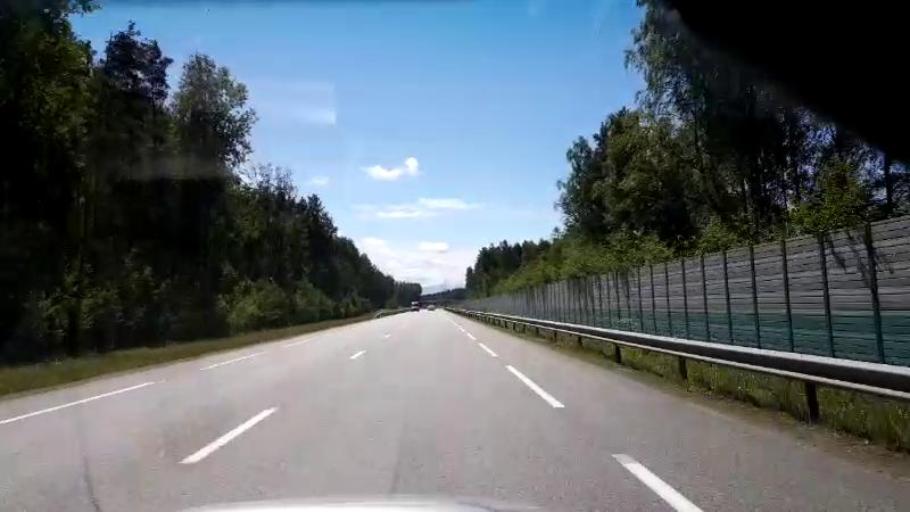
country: LV
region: Saulkrastu
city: Saulkrasti
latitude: 57.2499
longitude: 24.4281
